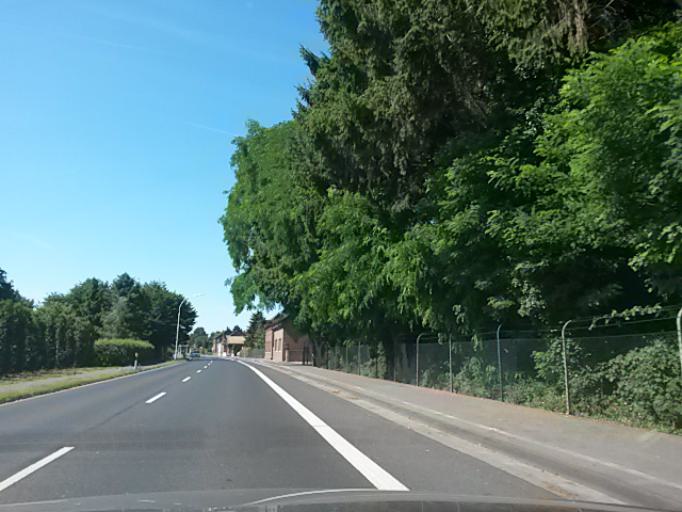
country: DE
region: North Rhine-Westphalia
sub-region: Regierungsbezirk Dusseldorf
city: Nettetal
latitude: 51.3003
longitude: 6.2589
